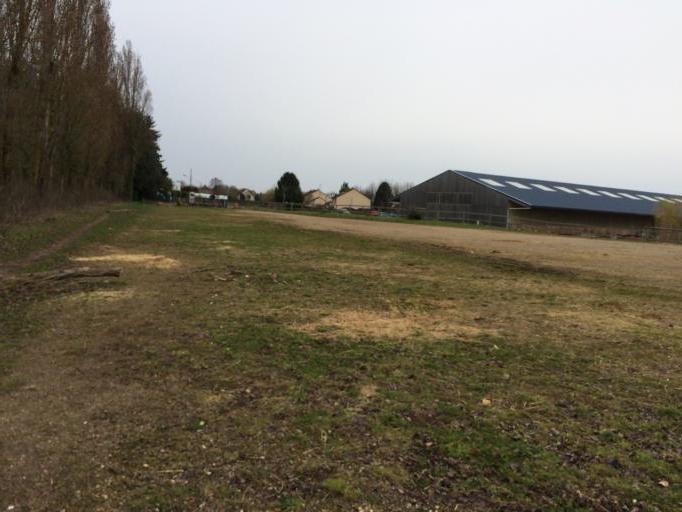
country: FR
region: Ile-de-France
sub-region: Departement des Yvelines
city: Les Loges-en-Josas
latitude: 48.7589
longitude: 2.1365
